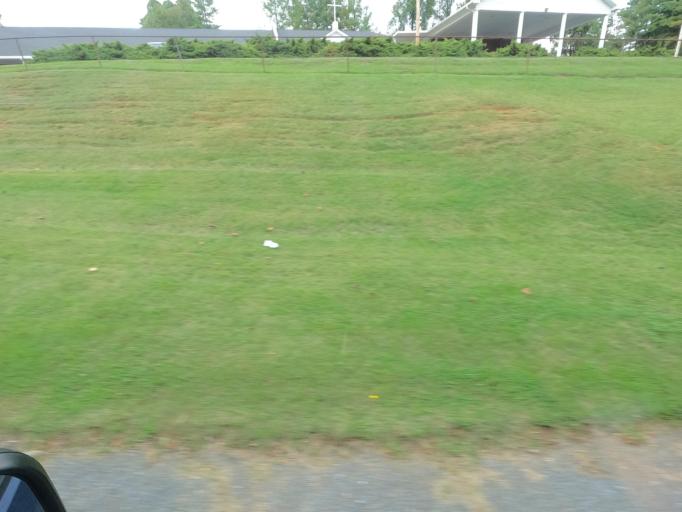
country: US
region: Tennessee
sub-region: Carter County
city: Central
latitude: 36.3271
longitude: -82.2727
